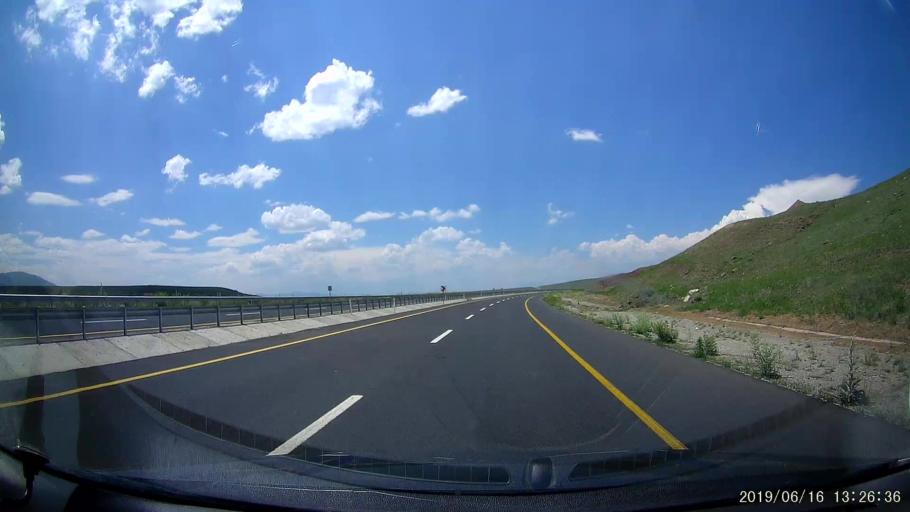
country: TR
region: Agri
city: Taslicay
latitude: 39.6598
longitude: 43.3246
